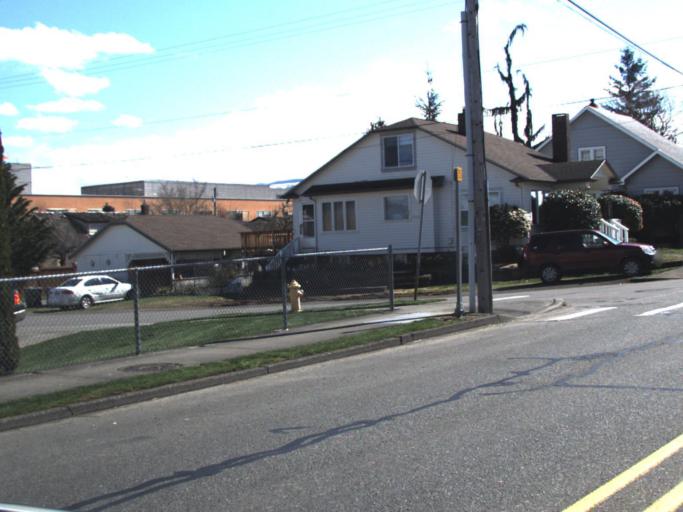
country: US
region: Washington
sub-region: King County
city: Enumclaw
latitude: 47.2105
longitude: -121.9896
